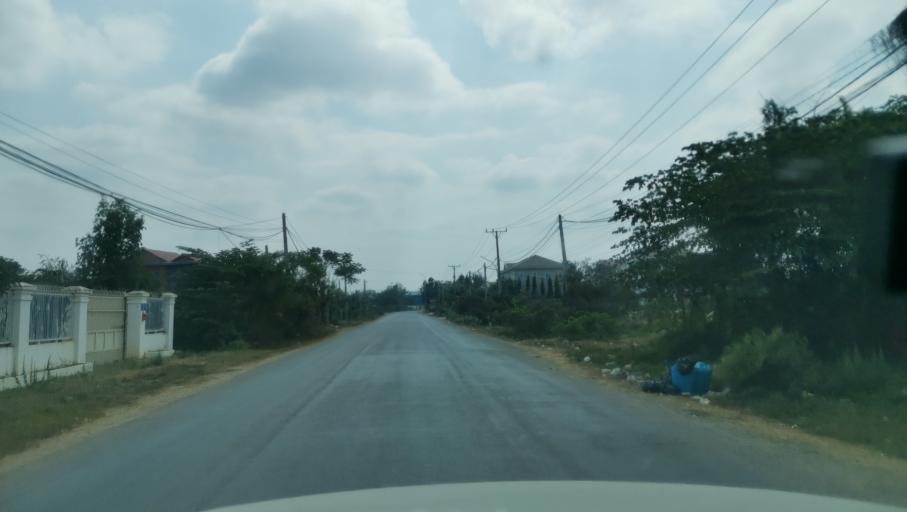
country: KH
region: Battambang
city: Battambang
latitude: 13.0801
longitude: 103.1858
